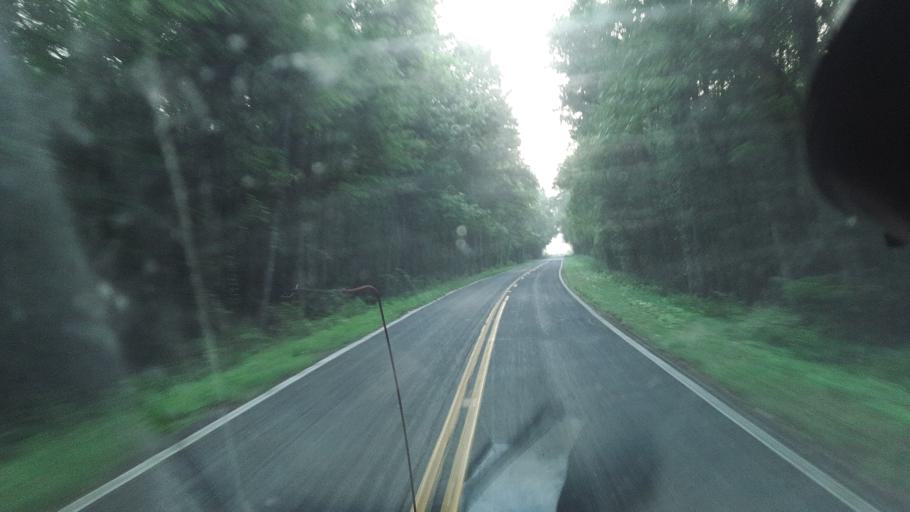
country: US
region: South Carolina
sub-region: Clarendon County
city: Manning
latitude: 33.7602
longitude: -80.0552
